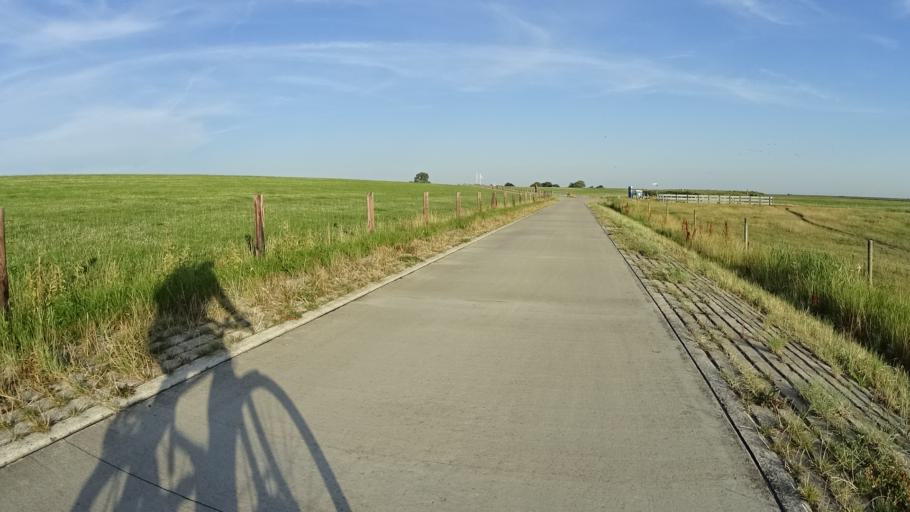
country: DE
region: Lower Saxony
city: Butjadingen
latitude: 53.6069
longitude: 8.3284
